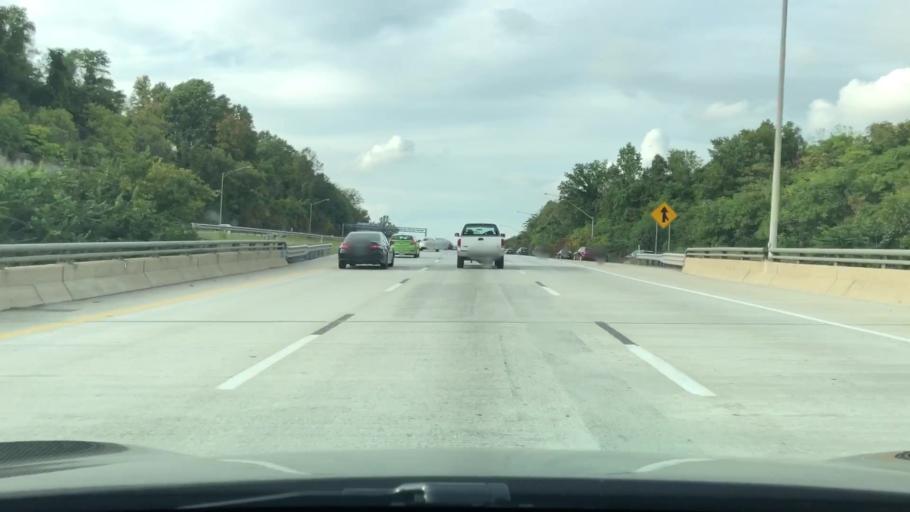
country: US
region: Pennsylvania
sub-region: Montgomery County
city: West Conshohocken
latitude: 40.0676
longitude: -75.3212
